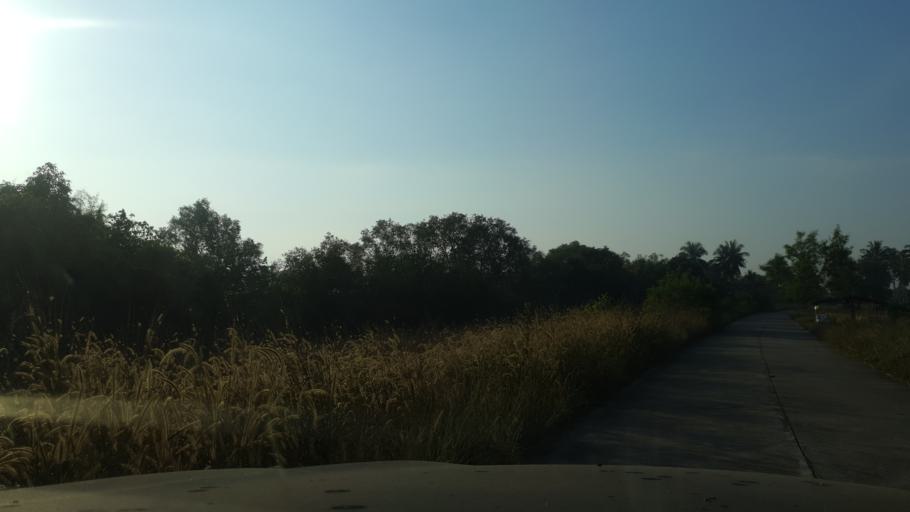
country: TH
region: Prachuap Khiri Khan
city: Bang Saphan
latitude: 11.2963
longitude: 99.5494
